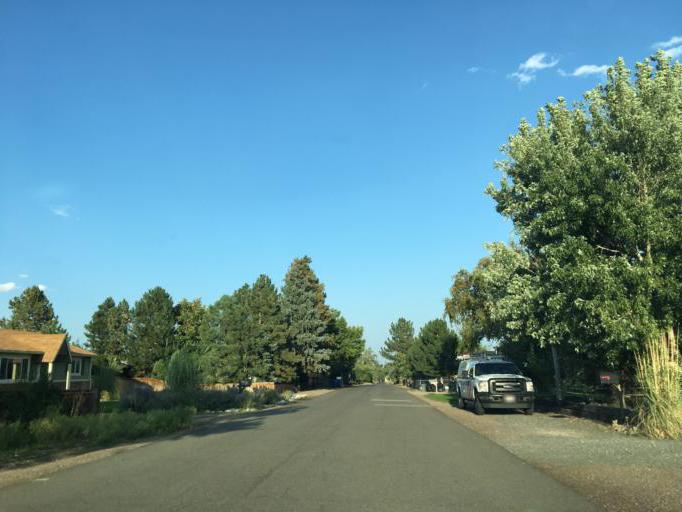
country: US
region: Colorado
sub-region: Jefferson County
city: Applewood
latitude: 39.7834
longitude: -105.1723
